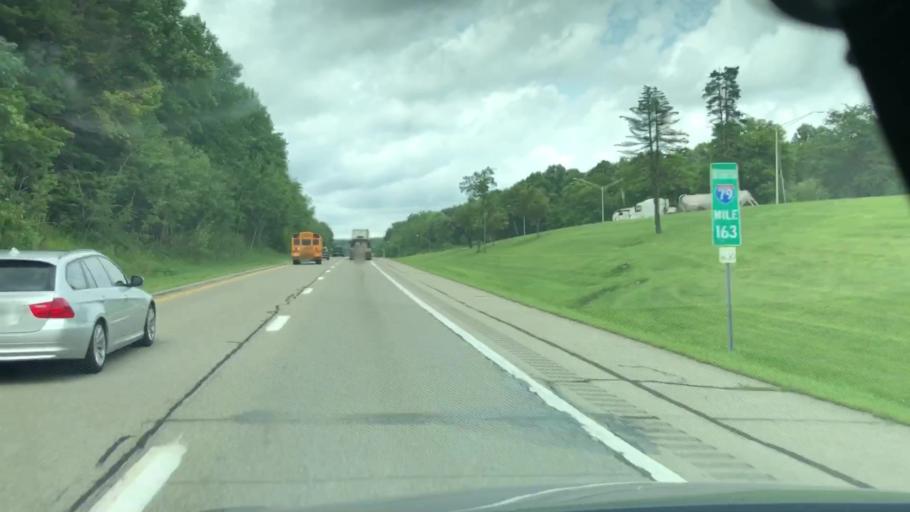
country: US
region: Pennsylvania
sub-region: Erie County
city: Edinboro
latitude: 41.8416
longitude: -80.1758
